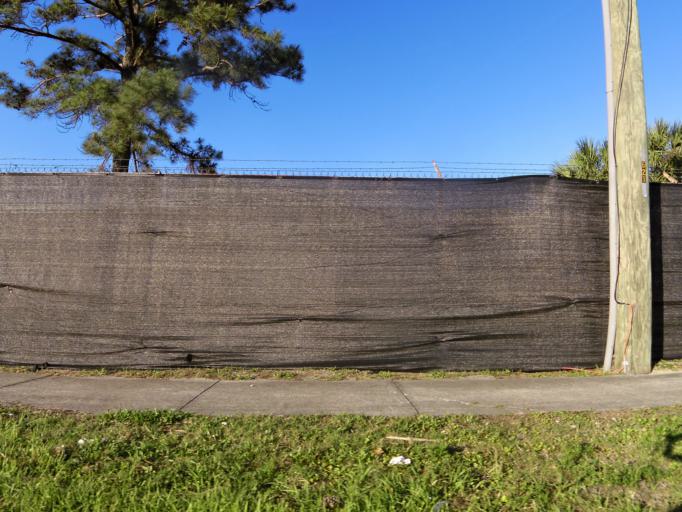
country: US
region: Florida
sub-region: Duval County
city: Jacksonville
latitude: 30.3344
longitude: -81.6823
